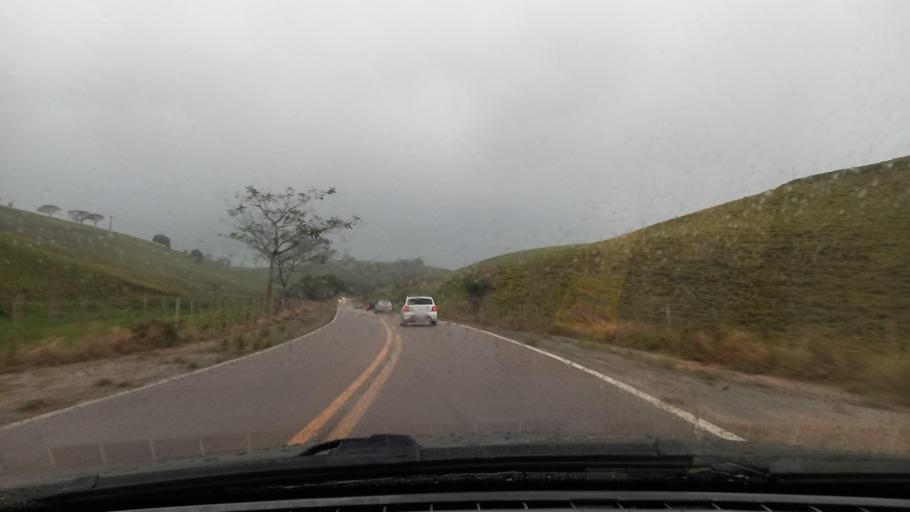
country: BR
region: Pernambuco
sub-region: Rio Formoso
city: Rio Formoso
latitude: -8.7428
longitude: -35.1741
